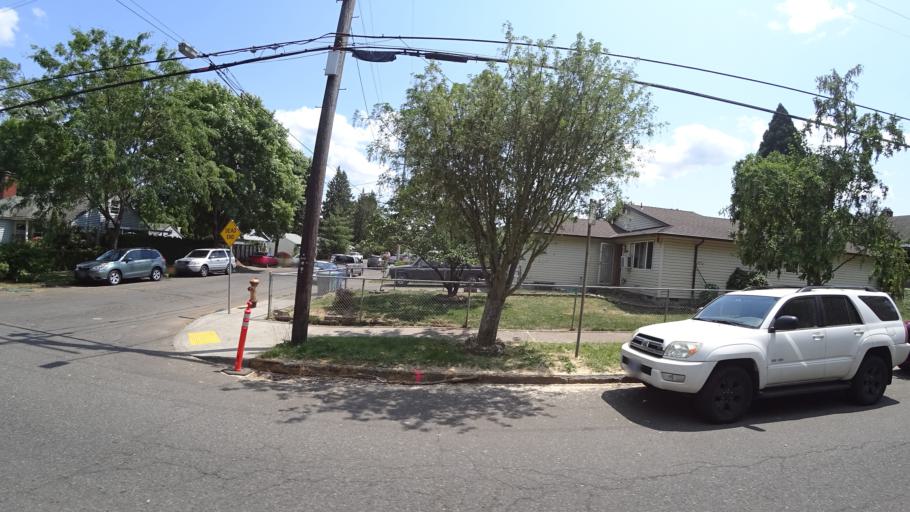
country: US
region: Oregon
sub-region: Washington County
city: West Haven
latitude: 45.5895
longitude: -122.7371
